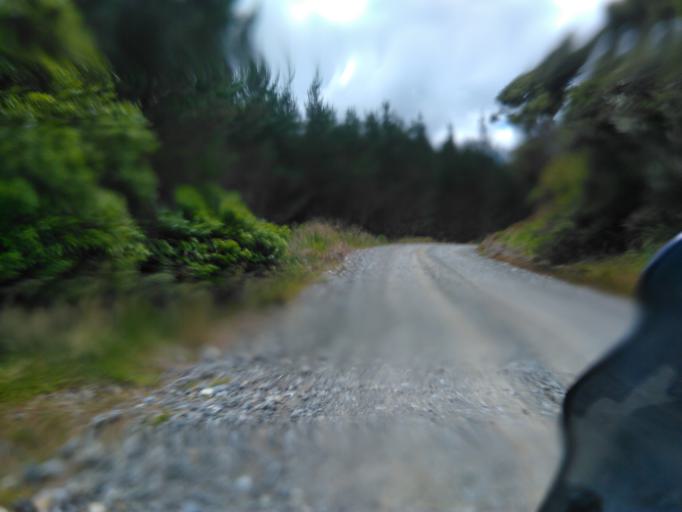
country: NZ
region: Gisborne
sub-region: Gisborne District
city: Gisborne
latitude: -38.1843
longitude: 178.1138
